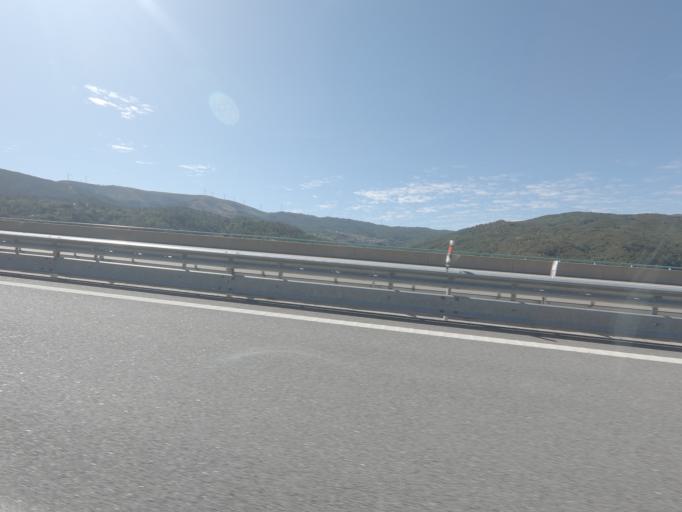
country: PT
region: Porto
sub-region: Baiao
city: Valadares
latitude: 41.2550
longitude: -7.9588
